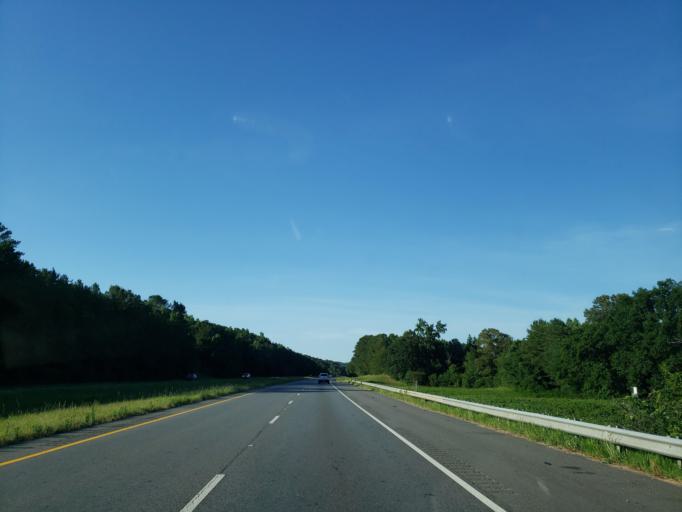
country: US
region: Georgia
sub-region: Floyd County
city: Shannon
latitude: 34.3083
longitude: -85.1121
